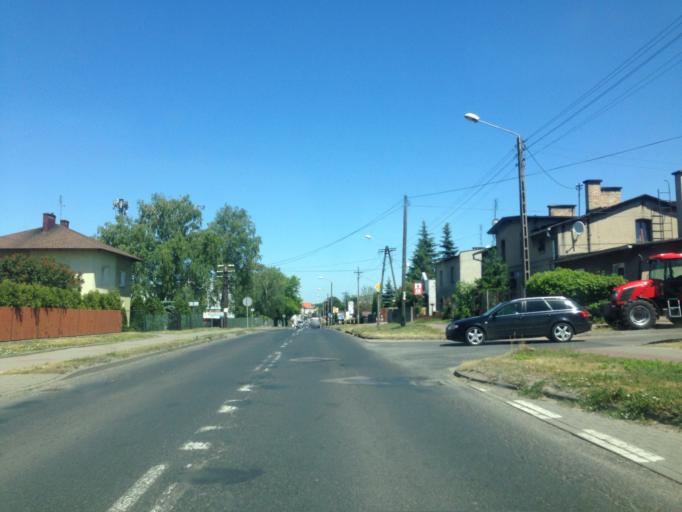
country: PL
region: Kujawsko-Pomorskie
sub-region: Powiat brodnicki
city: Brodnica
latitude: 53.2439
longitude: 19.3961
